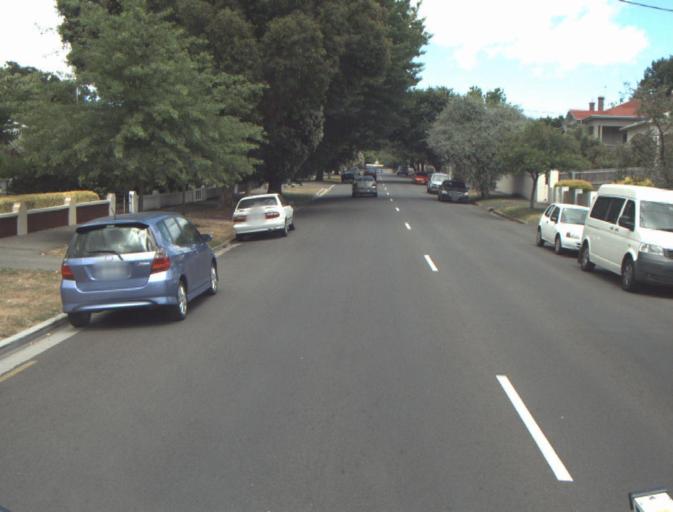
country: AU
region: Tasmania
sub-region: Launceston
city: East Launceston
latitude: -41.4421
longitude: 147.1598
